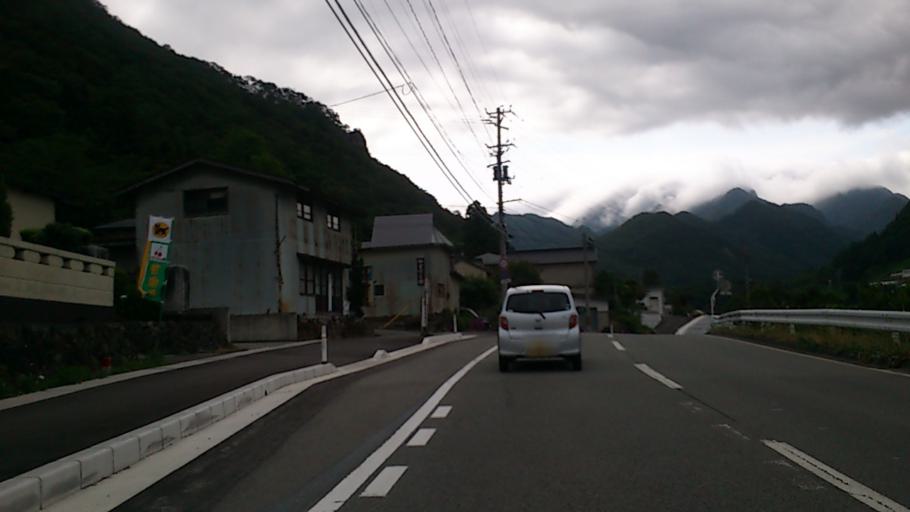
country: JP
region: Yamagata
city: Tendo
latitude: 38.3120
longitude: 140.4235
